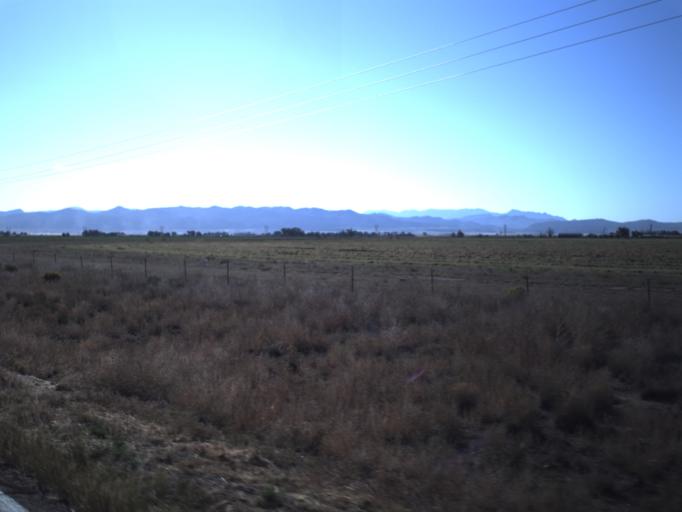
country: US
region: Utah
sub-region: Washington County
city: Enterprise
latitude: 37.7172
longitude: -113.6777
